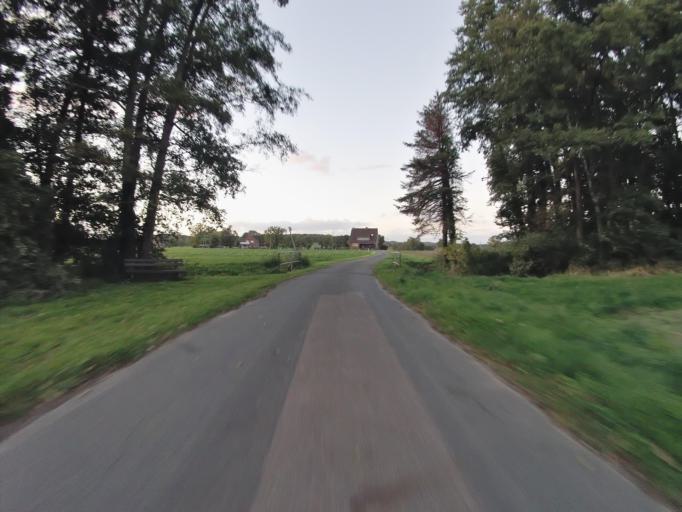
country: DE
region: North Rhine-Westphalia
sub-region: Regierungsbezirk Munster
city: Tecklenburg
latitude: 52.2427
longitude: 7.8084
